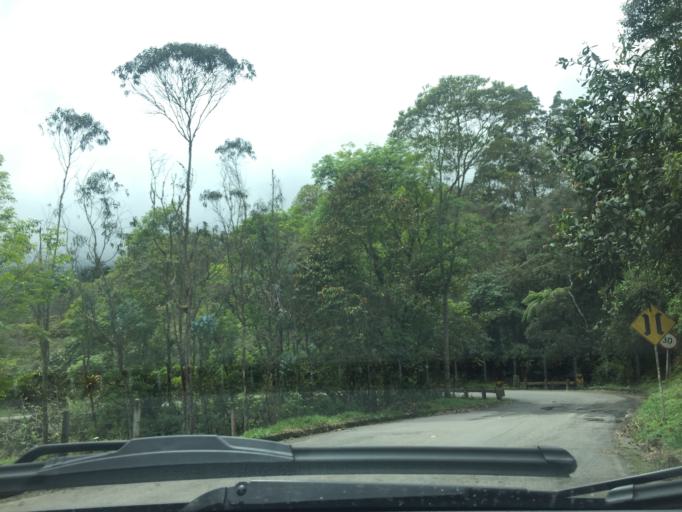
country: CO
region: Cundinamarca
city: Supata
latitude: 5.0526
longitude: -74.2407
